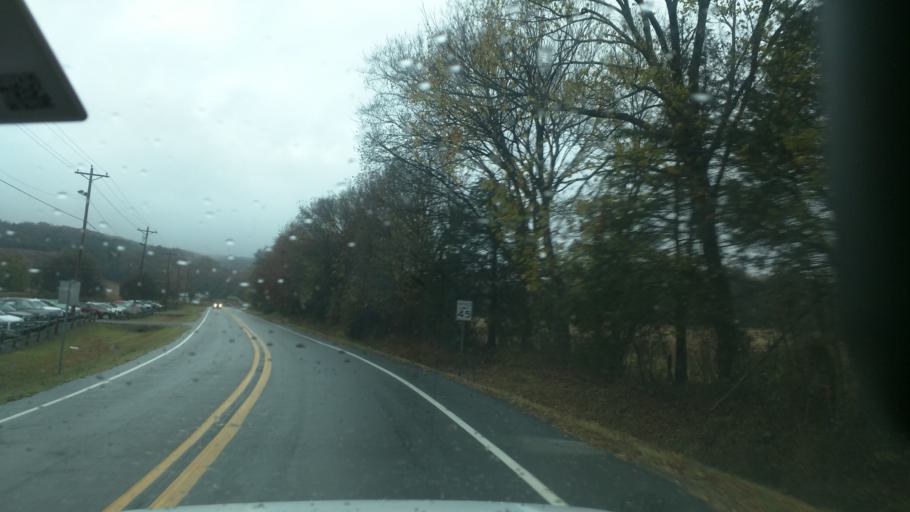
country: US
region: Arkansas
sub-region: Franklin County
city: Ozark
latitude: 35.5085
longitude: -93.8461
